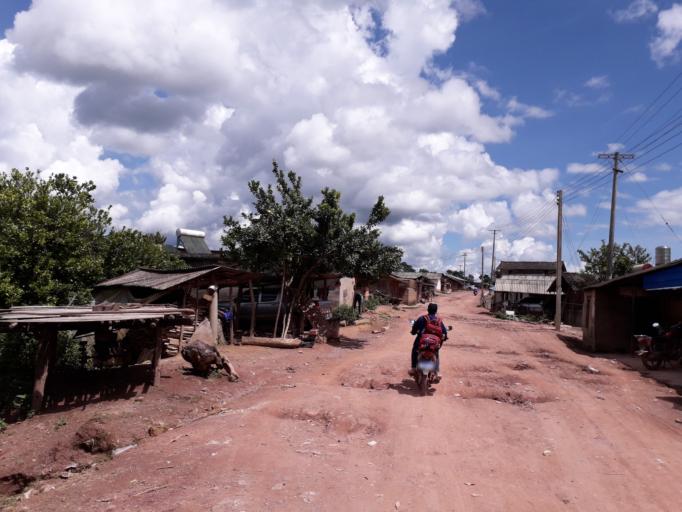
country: CN
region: Yunnan
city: Menglie
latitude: 22.2655
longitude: 101.5736
